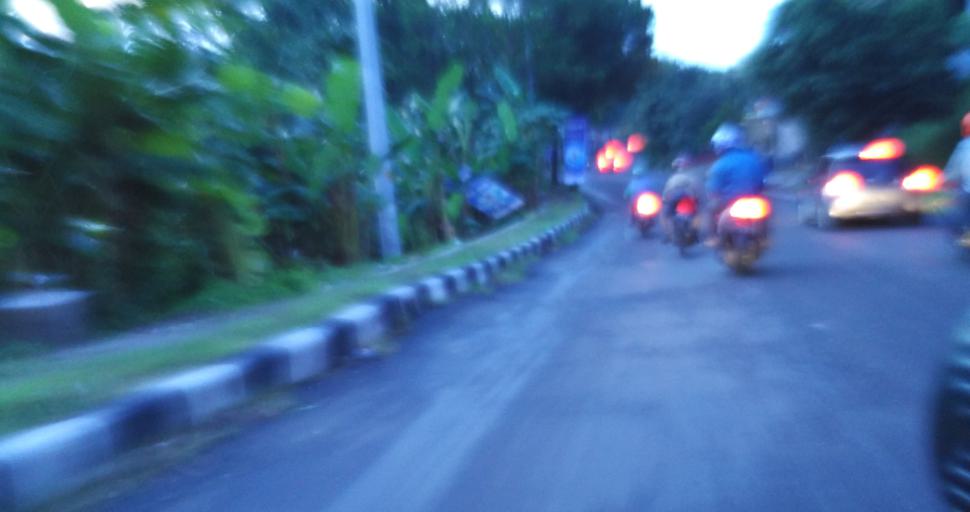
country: ID
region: Central Java
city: Semarang
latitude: -7.0411
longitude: 110.4199
